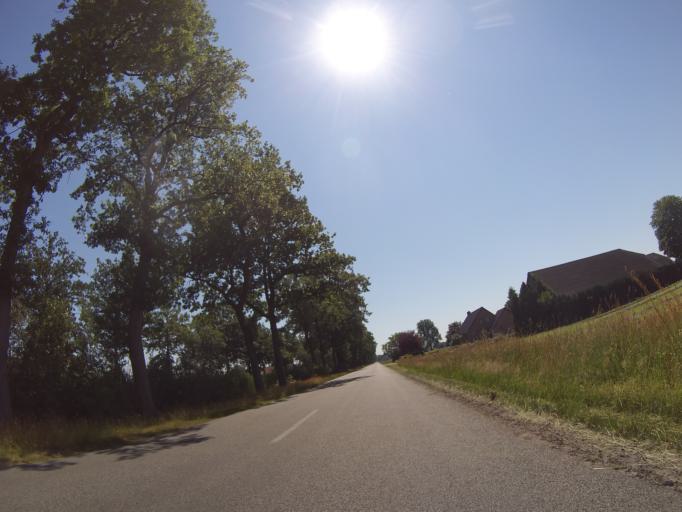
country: NL
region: Drenthe
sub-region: Gemeente Borger-Odoorn
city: Borger
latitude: 52.8488
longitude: 6.7747
